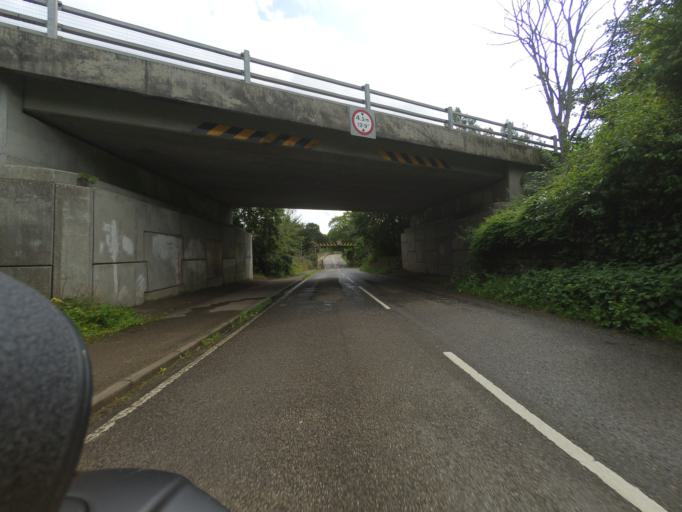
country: GB
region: Scotland
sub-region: Highland
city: Tain
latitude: 57.7456
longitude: -4.0745
